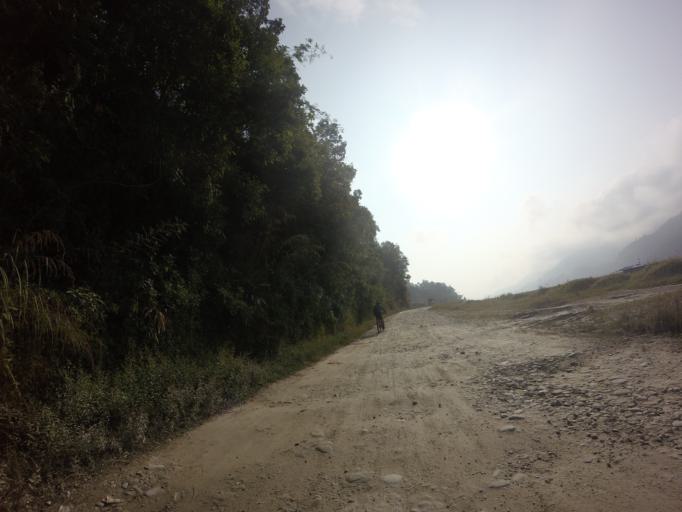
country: NP
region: Western Region
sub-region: Gandaki Zone
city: Pokhara
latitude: 28.2348
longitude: 83.9139
